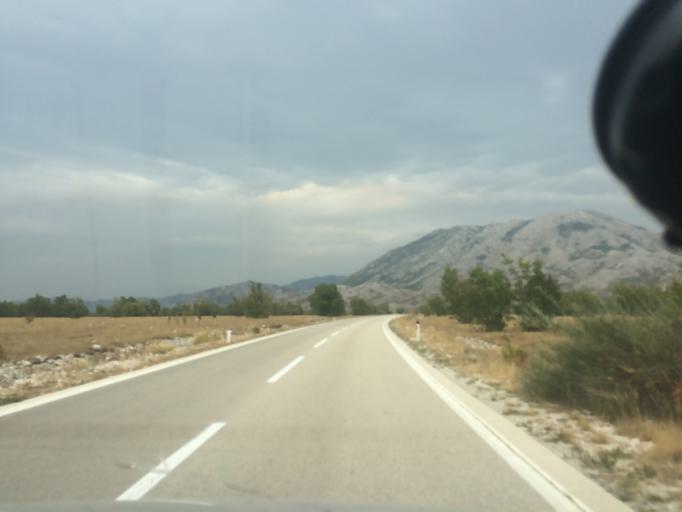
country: ME
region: Kotor
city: Risan
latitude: 42.5866
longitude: 18.6866
